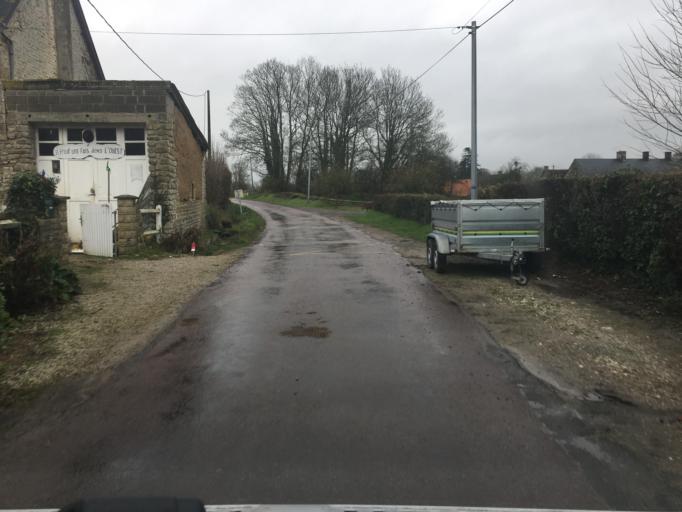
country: FR
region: Lower Normandy
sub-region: Departement de la Manche
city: Sainte-Mere-Eglise
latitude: 49.4268
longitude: -1.2644
